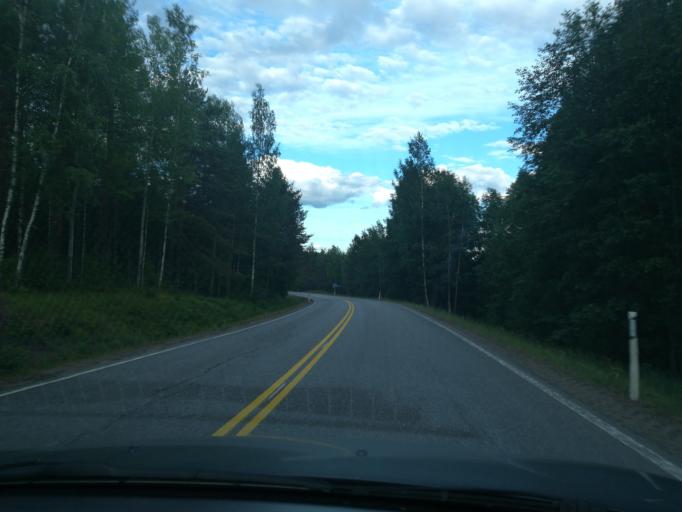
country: FI
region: Southern Savonia
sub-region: Mikkeli
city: Puumala
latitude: 61.5627
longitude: 28.1053
